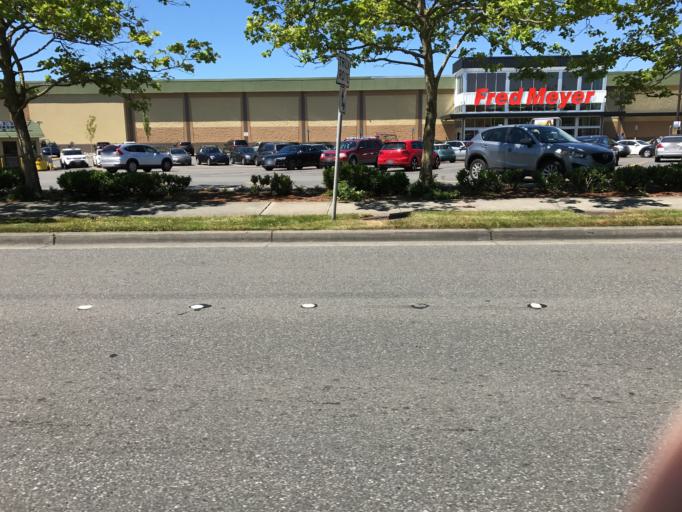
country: US
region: Washington
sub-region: King County
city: Redmond
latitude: 47.6289
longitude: -122.1431
